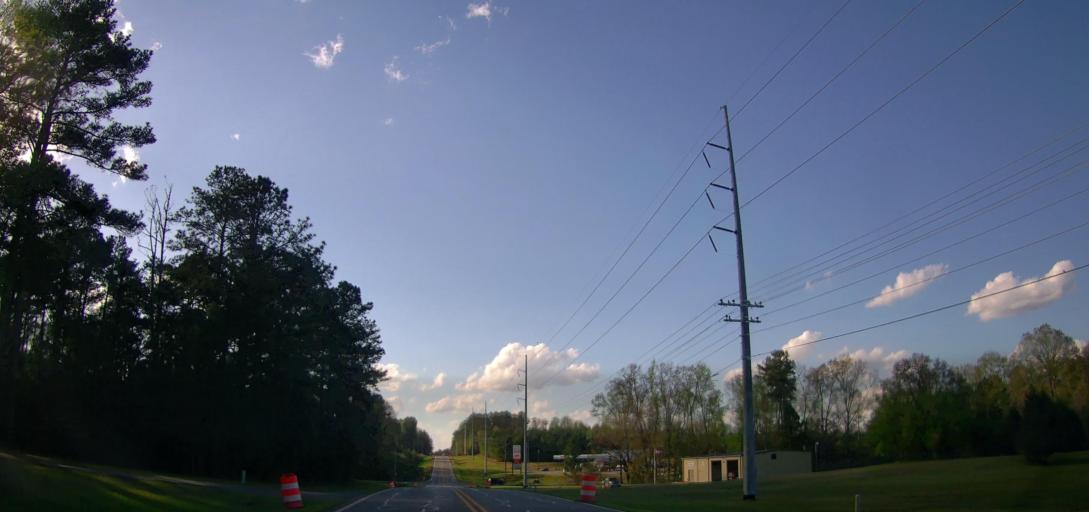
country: US
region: Georgia
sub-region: Baldwin County
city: Milledgeville
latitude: 33.1529
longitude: -83.3463
